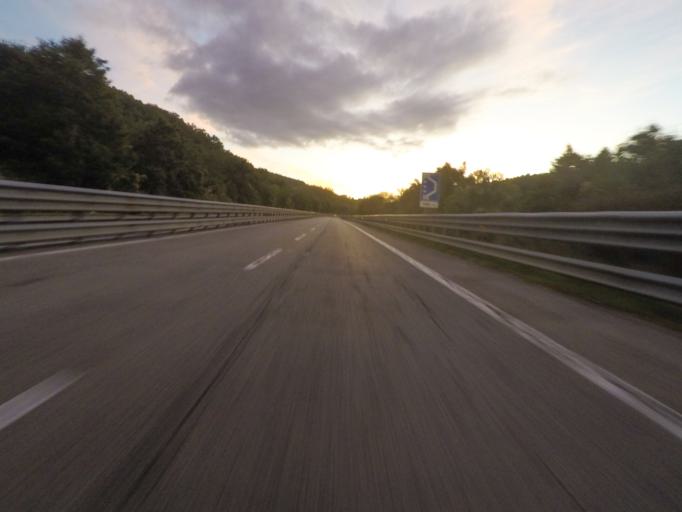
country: IT
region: Tuscany
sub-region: Province of Arezzo
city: Lucignano
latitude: 43.2555
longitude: 11.6881
